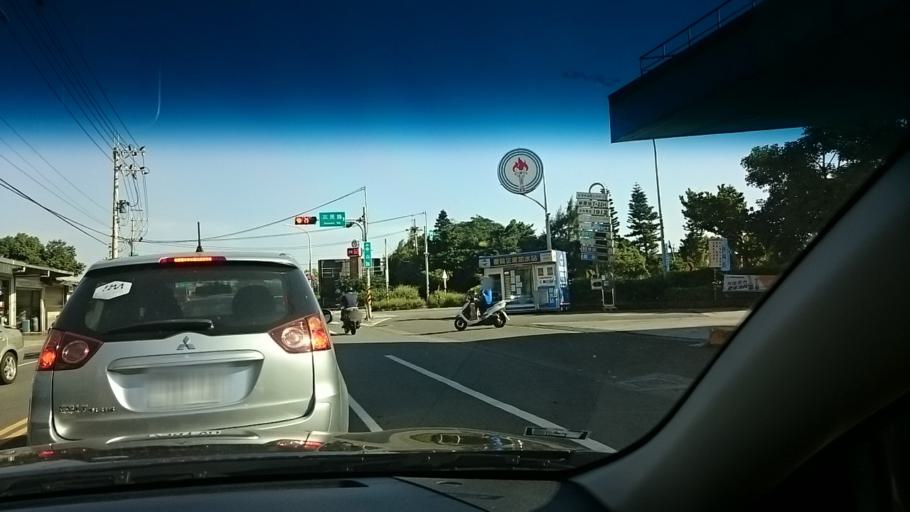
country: TW
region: Taiwan
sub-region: Hsinchu
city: Zhubei
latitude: 24.9711
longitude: 121.1106
